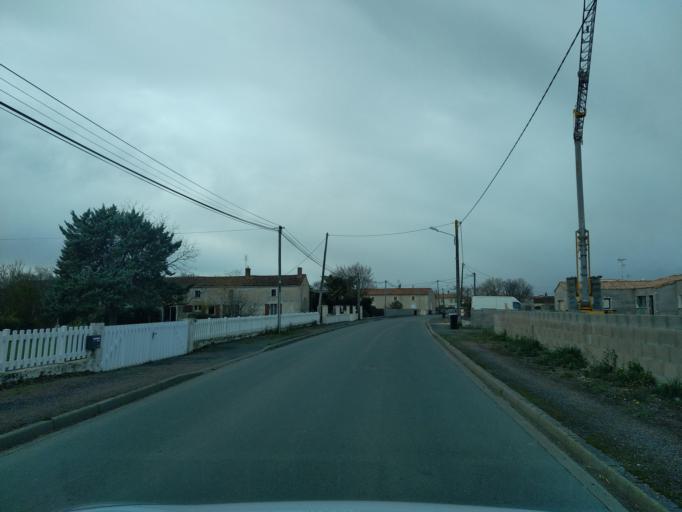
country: FR
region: Pays de la Loire
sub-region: Departement de la Vendee
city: Vix
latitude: 46.3538
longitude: -0.8437
